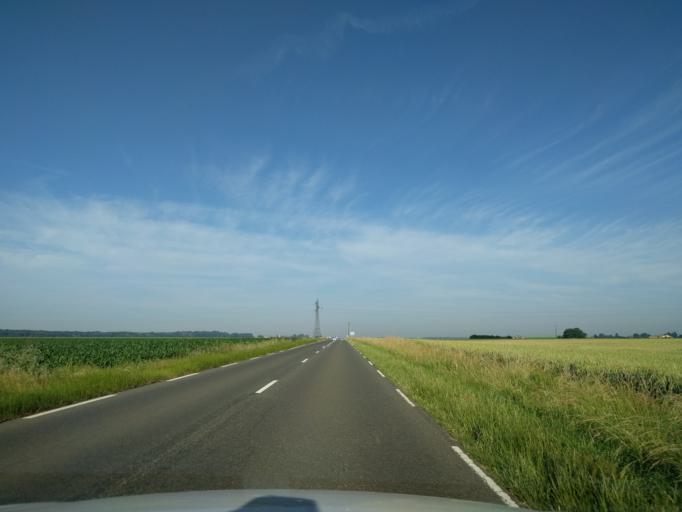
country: FR
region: Picardie
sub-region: Departement de l'Oise
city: Ansauvillers
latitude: 49.6316
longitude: 2.4442
